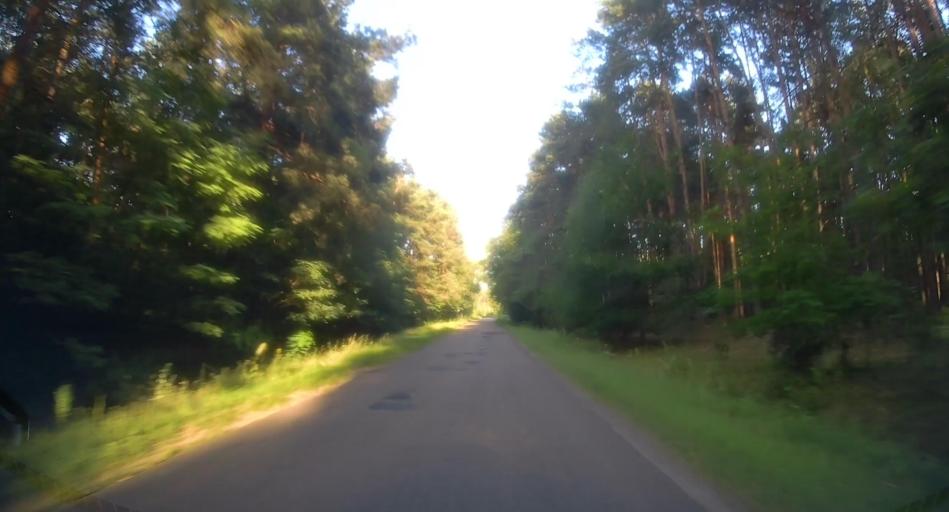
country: PL
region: Lodz Voivodeship
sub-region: Powiat skierniewicki
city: Kowiesy
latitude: 51.9062
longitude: 20.3509
